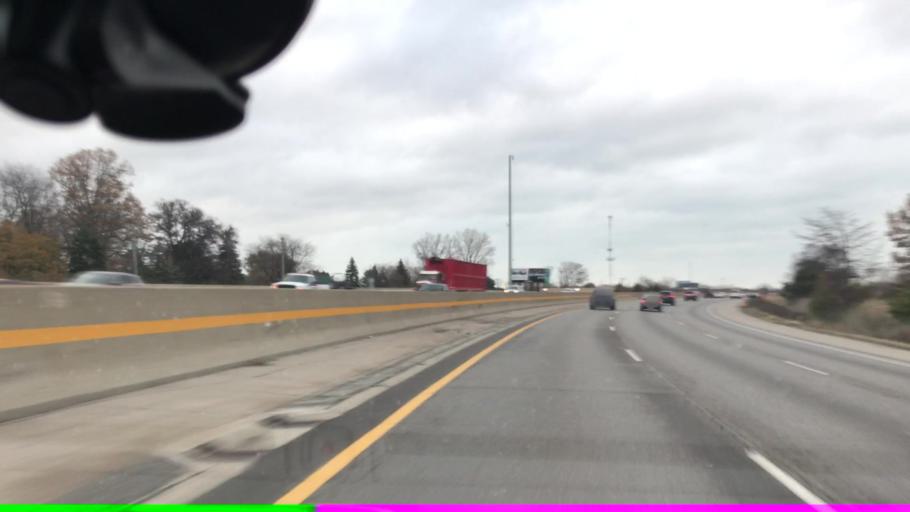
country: US
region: Michigan
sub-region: Macomb County
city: Saint Clair Shores
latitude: 42.5393
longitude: -82.8983
